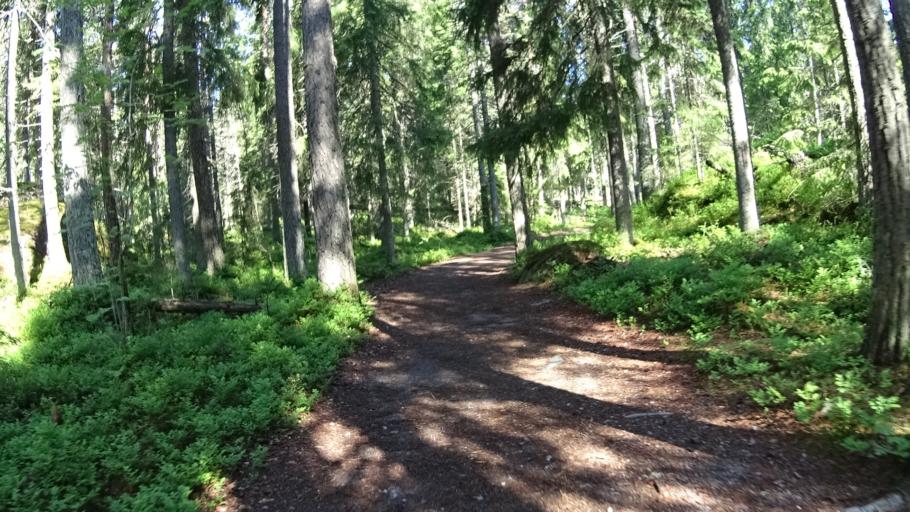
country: FI
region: Uusimaa
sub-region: Helsinki
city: Kauniainen
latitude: 60.3245
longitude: 24.6865
